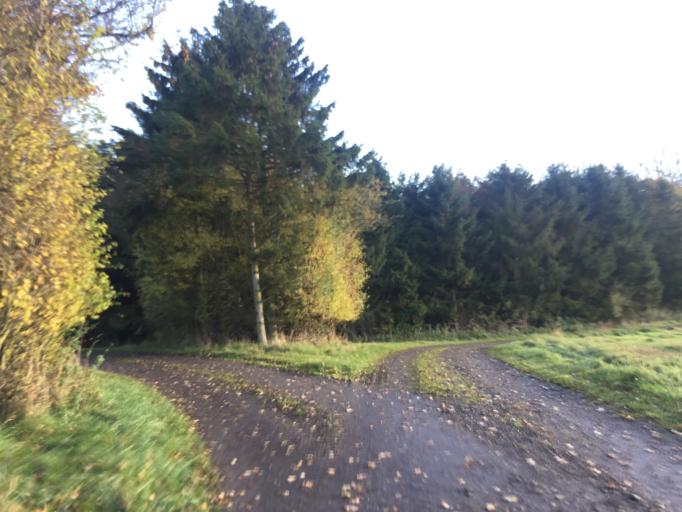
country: DK
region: Zealand
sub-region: Ringsted Kommune
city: Ringsted
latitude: 55.4713
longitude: 11.7633
